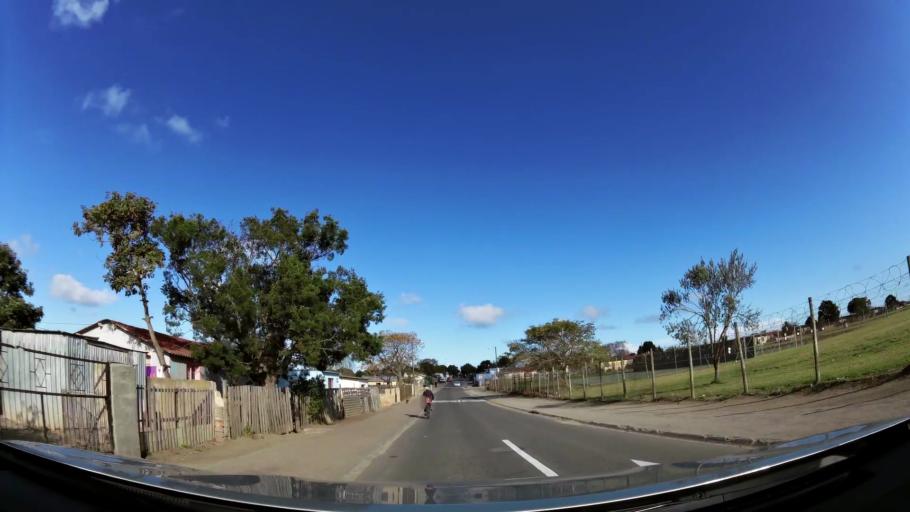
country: ZA
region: Western Cape
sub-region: Eden District Municipality
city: George
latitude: -33.9833
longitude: 22.4755
